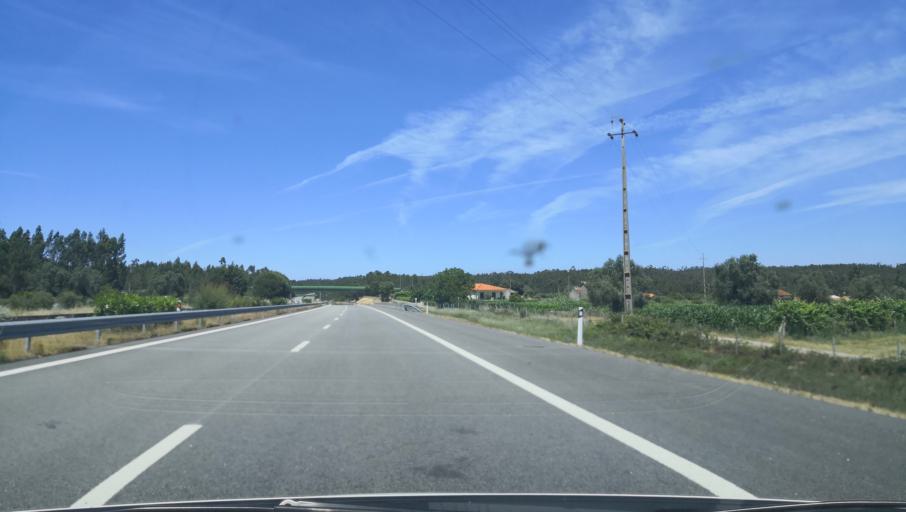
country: PT
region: Coimbra
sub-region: Montemor-O-Velho
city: Arazede
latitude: 40.2348
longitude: -8.6637
